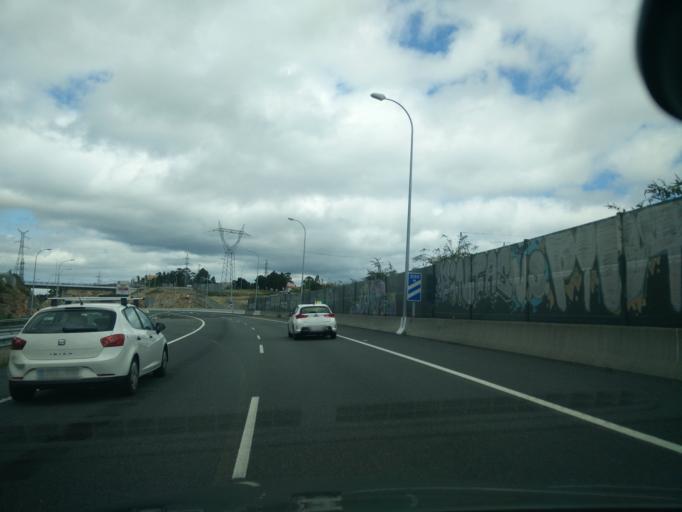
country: ES
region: Galicia
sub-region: Provincia da Coruna
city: Culleredo
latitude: 43.3205
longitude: -8.4088
